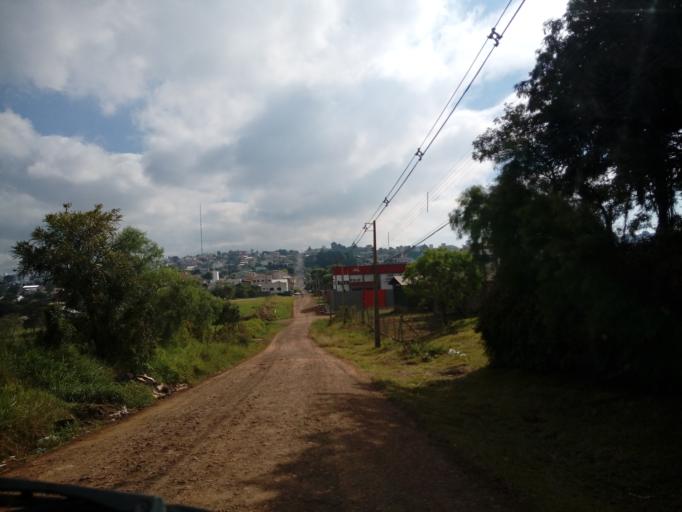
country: BR
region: Santa Catarina
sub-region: Chapeco
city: Chapeco
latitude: -27.0996
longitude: -52.5942
